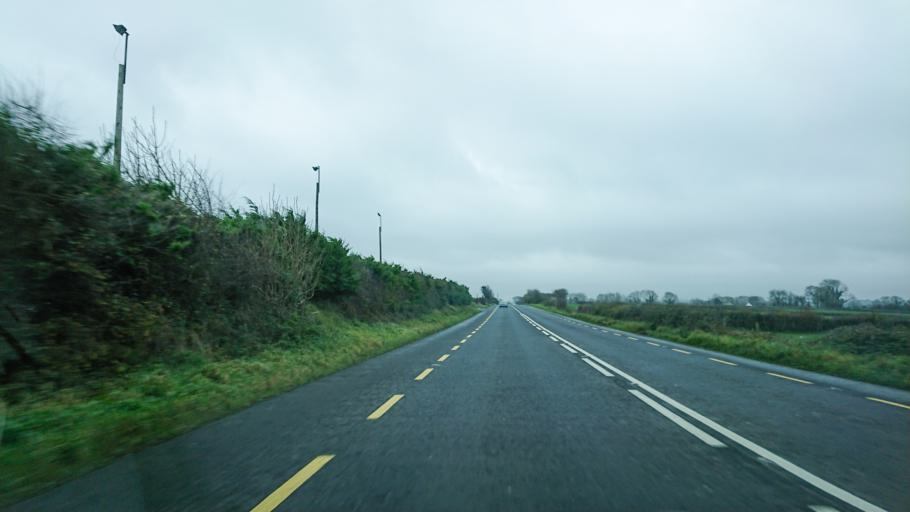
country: IE
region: Leinster
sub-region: Kilkenny
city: Mooncoin
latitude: 52.2878
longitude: -7.2240
